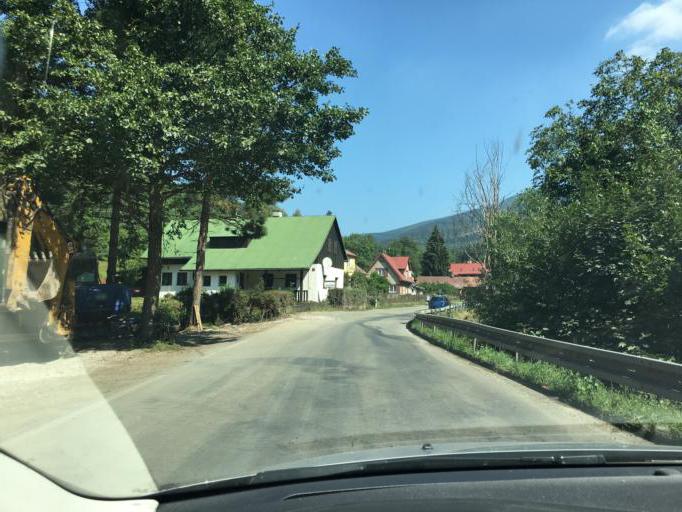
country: CZ
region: Kralovehradecky
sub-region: Okres Trutnov
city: Rudnik
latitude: 50.6232
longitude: 15.7115
